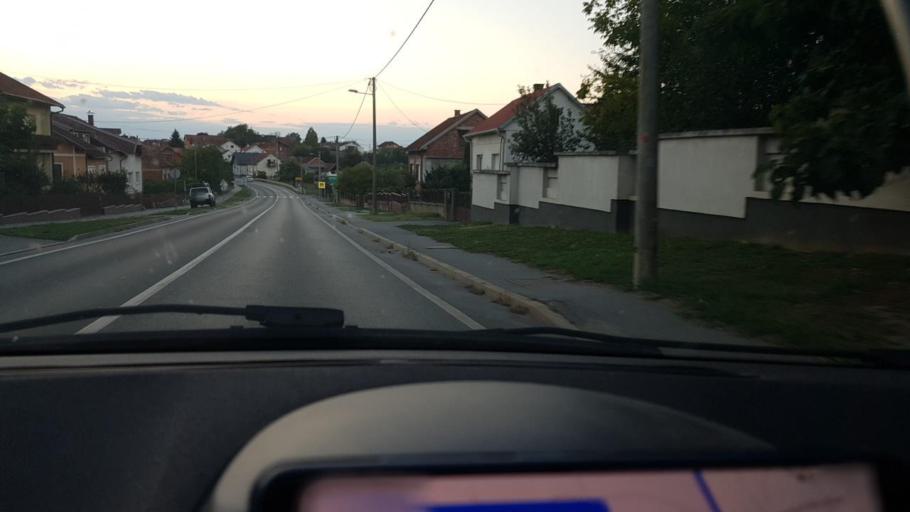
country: HR
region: Bjelovarsko-Bilogorska
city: Zdralovi
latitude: 45.8855
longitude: 16.8643
